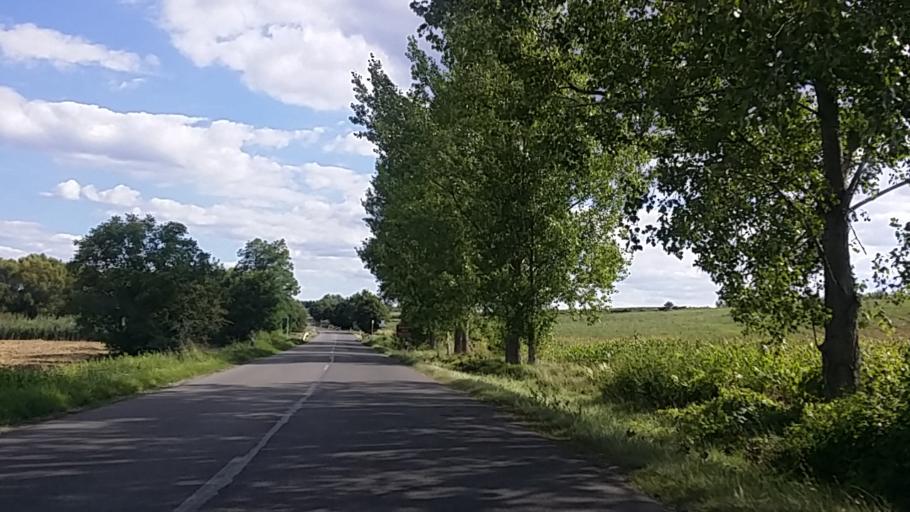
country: HU
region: Tolna
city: Dombovar
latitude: 46.3234
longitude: 18.1301
